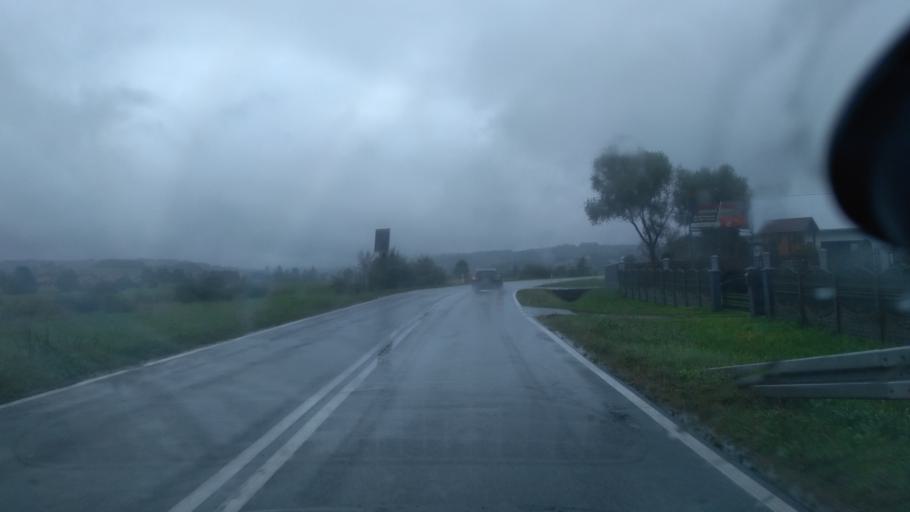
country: PL
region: Subcarpathian Voivodeship
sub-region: Powiat ropczycko-sedziszowski
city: Niedzwiada
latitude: 49.9814
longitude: 21.5594
